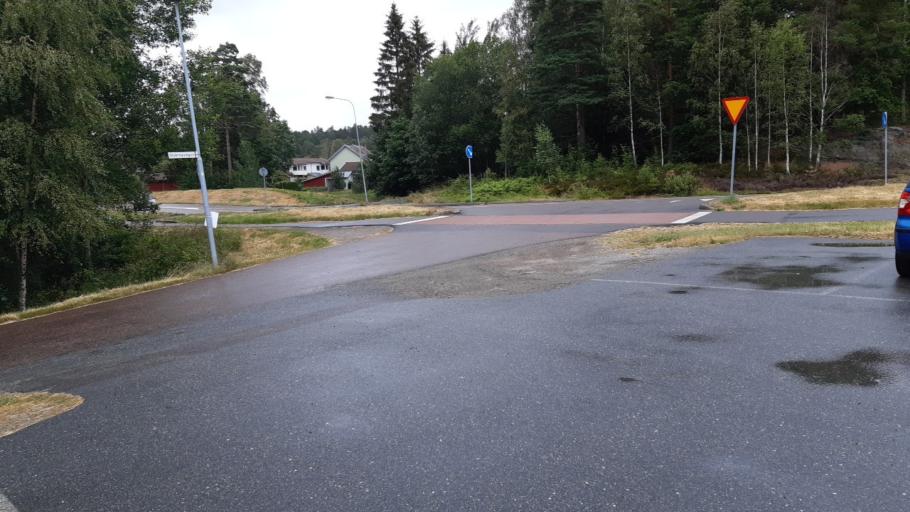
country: SE
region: Vaestra Goetaland
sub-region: Harryda Kommun
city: Molnlycke
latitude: 57.6497
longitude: 12.1419
